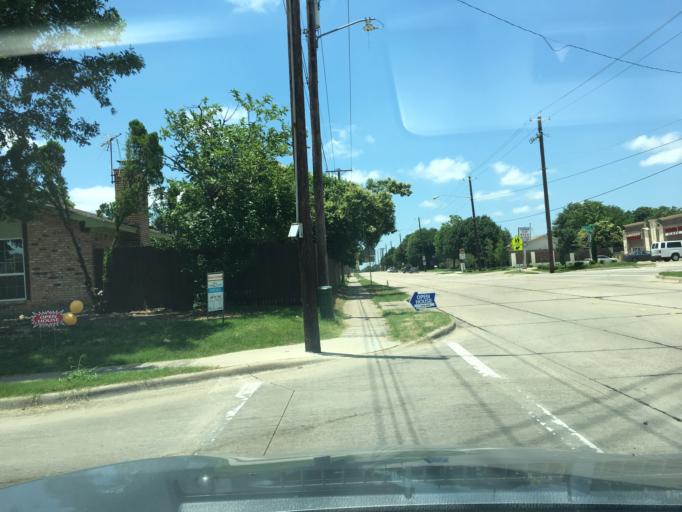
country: US
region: Texas
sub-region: Dallas County
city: Garland
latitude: 32.9514
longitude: -96.6735
